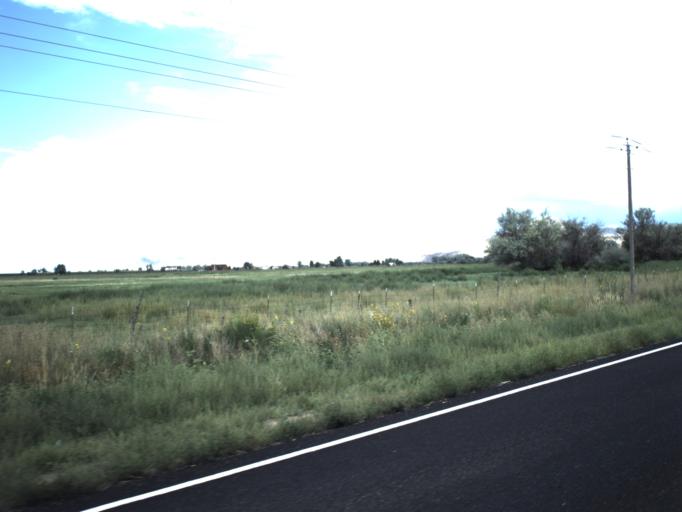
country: US
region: Utah
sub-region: Sevier County
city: Richfield
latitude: 38.7732
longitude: -112.0454
